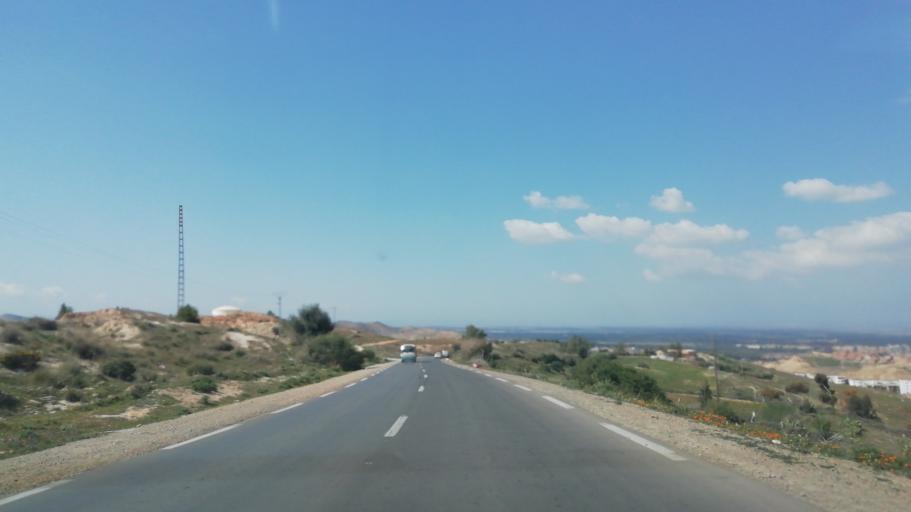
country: DZ
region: Mascara
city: Mascara
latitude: 35.5544
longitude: 0.0804
